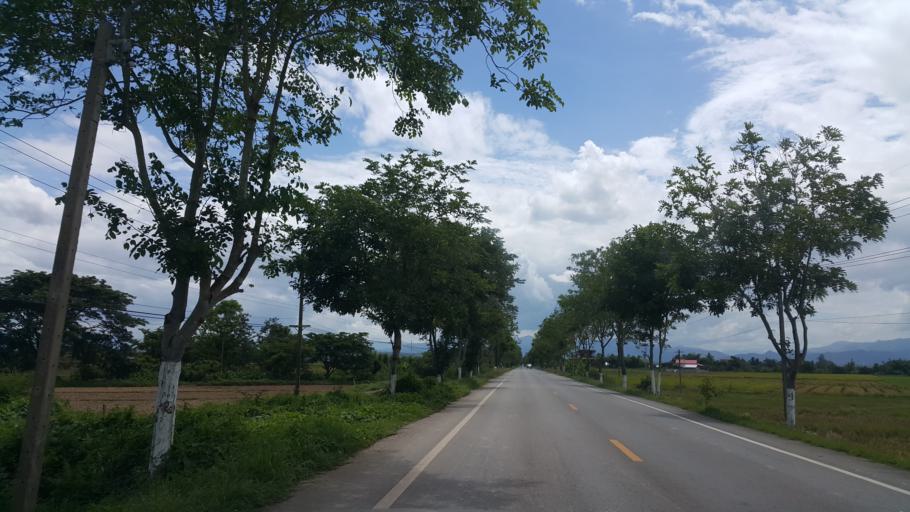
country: TH
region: Chiang Mai
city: Mae Taeng
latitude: 19.1429
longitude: 99.0310
